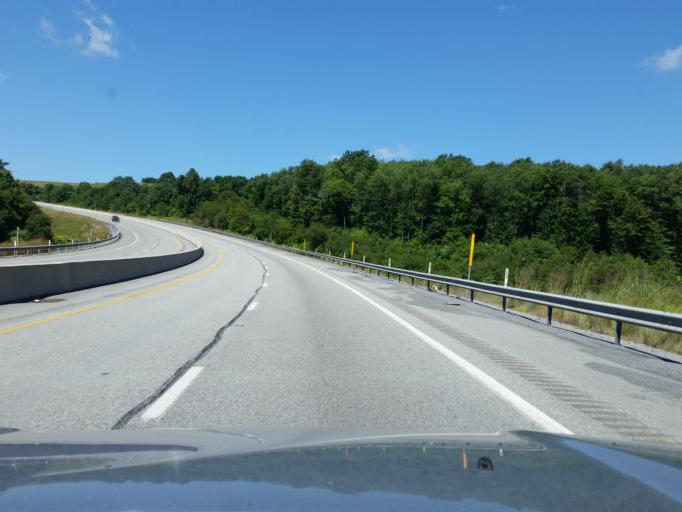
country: US
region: Pennsylvania
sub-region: Cambria County
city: Mundys Corner
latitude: 40.4518
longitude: -78.8713
